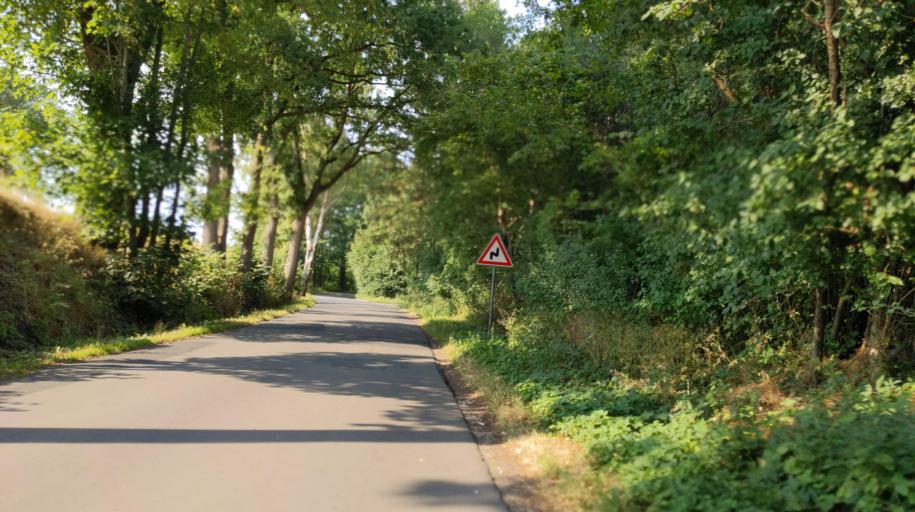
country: DE
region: Schleswig-Holstein
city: Rondeshagen
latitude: 53.7637
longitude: 10.6271
